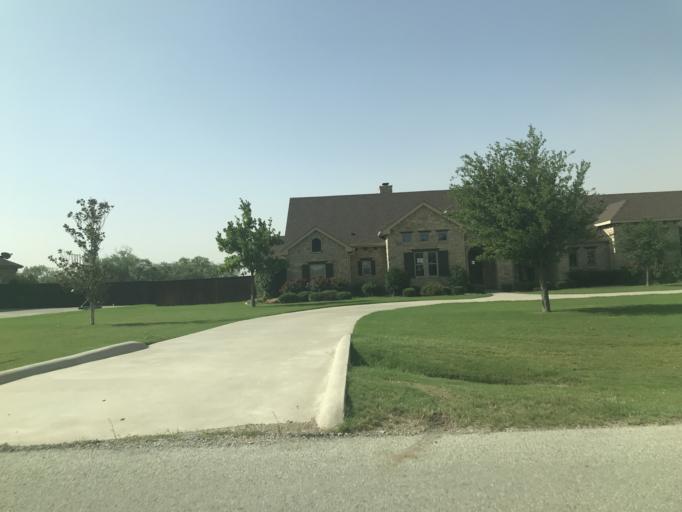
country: US
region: Texas
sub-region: Taylor County
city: Potosi
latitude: 32.3505
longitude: -99.7105
